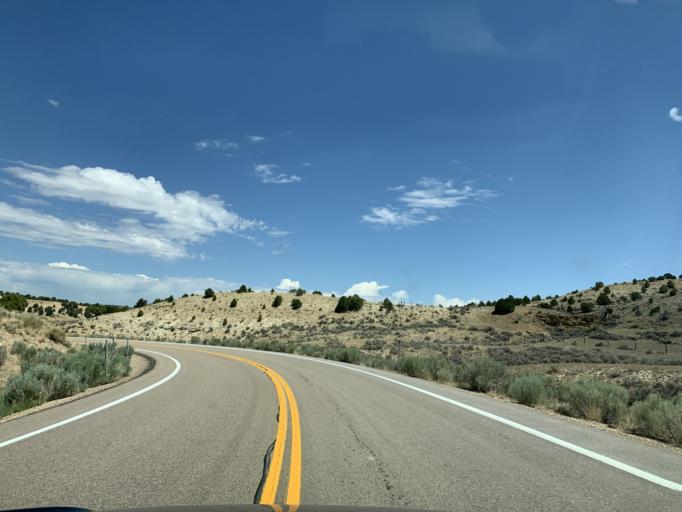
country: US
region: Utah
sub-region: Duchesne County
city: Duchesne
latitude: 39.8995
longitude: -110.2345
